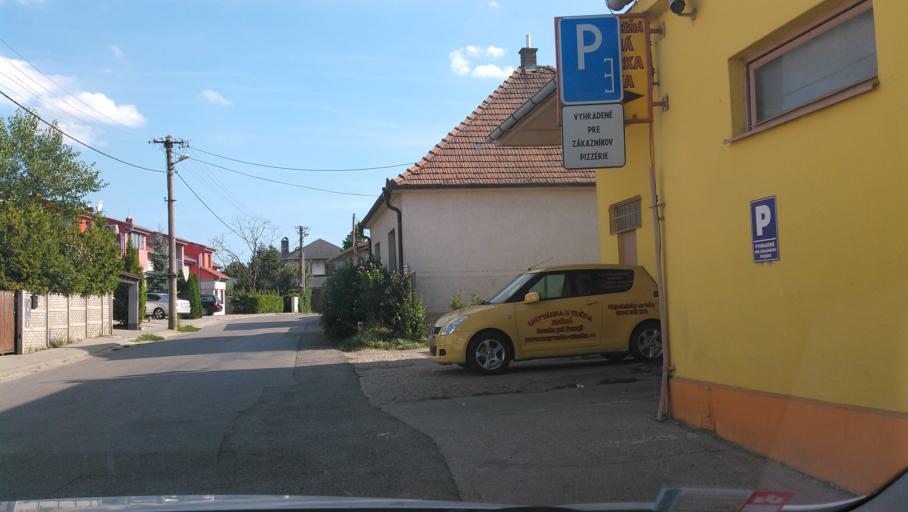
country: SK
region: Bratislavsky
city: Svaty Jur
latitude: 48.1888
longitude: 17.2505
